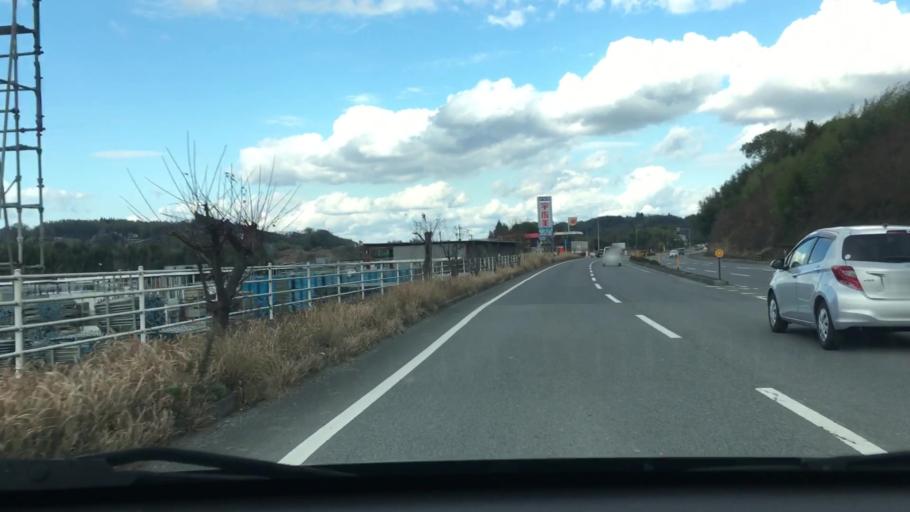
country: JP
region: Oita
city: Oita
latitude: 33.1234
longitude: 131.6544
